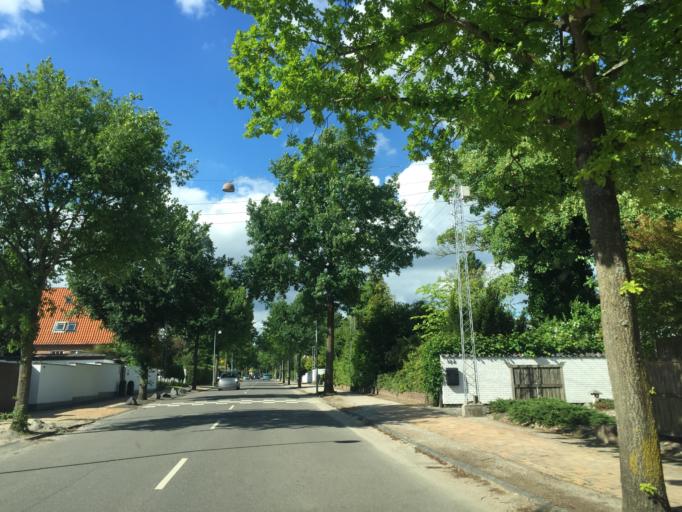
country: DK
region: South Denmark
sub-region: Odense Kommune
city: Odense
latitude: 55.3780
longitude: 10.3887
